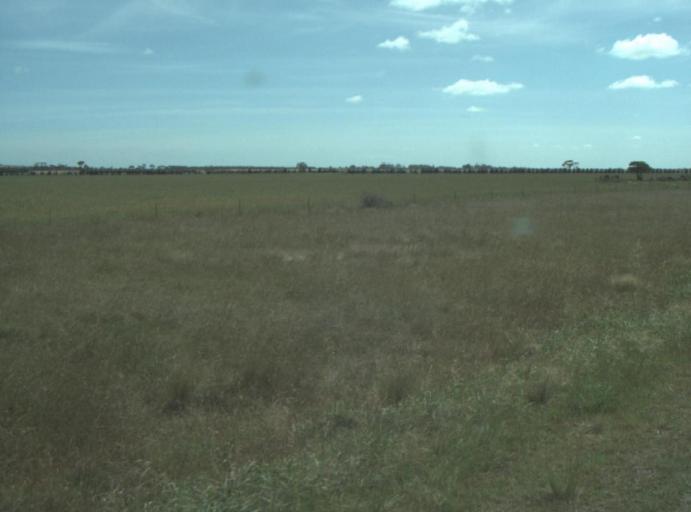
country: AU
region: Victoria
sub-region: Wyndham
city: Little River
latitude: -38.0073
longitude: 144.4631
